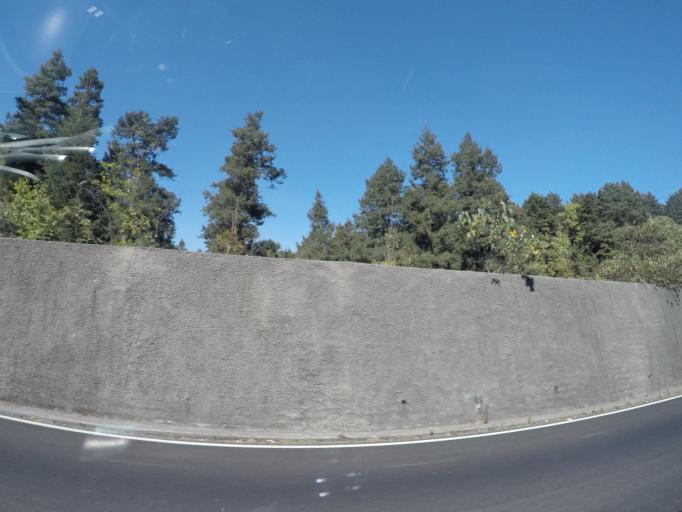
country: MX
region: Mexico City
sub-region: Cuajimalpa de Morelos
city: San Lorenzo Acopilco
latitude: 19.3168
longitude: -99.3262
